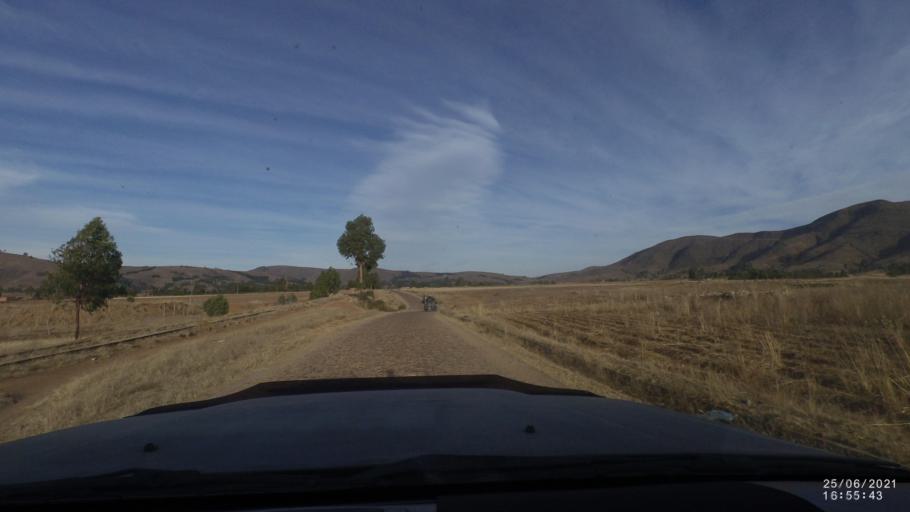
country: BO
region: Cochabamba
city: Arani
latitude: -17.8221
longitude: -65.7723
